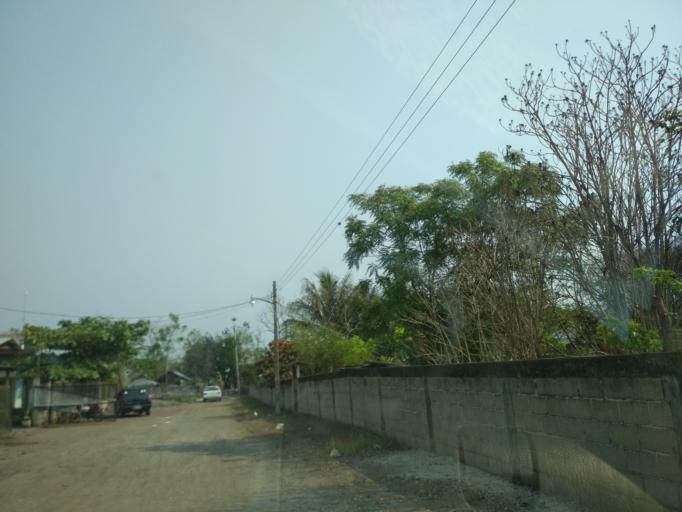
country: MX
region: Oaxaca
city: Acatlan de Perez Figueroa
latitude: 18.6071
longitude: -96.5765
